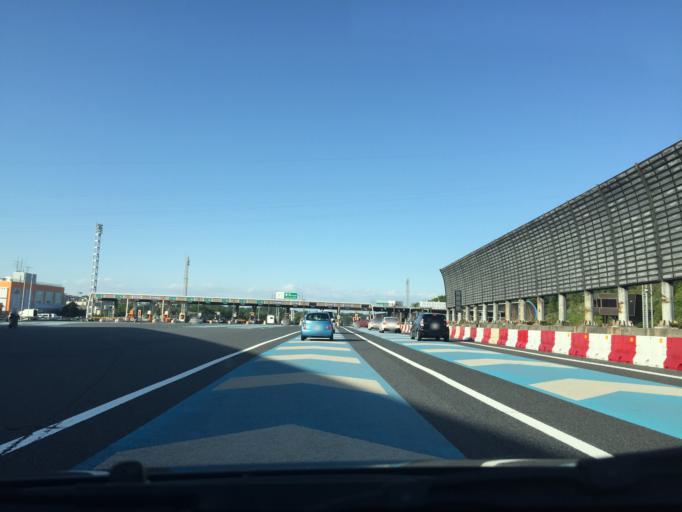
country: JP
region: Tokyo
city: Chofugaoka
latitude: 35.5929
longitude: 139.5719
